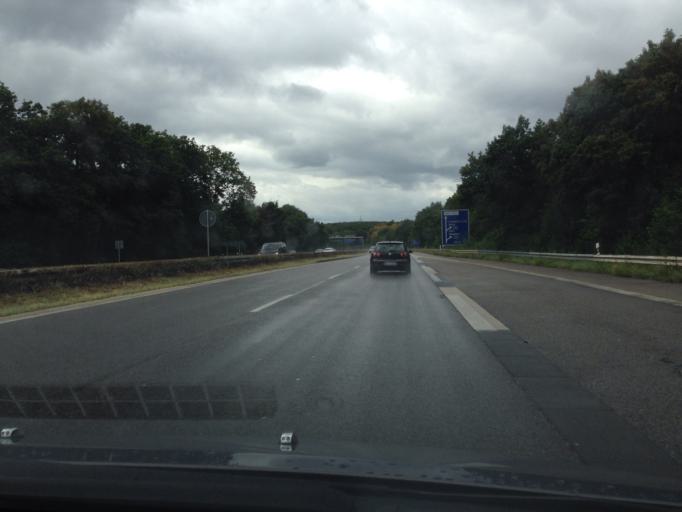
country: DE
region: North Rhine-Westphalia
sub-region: Regierungsbezirk Koln
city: Eil
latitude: 50.8843
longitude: 7.1033
